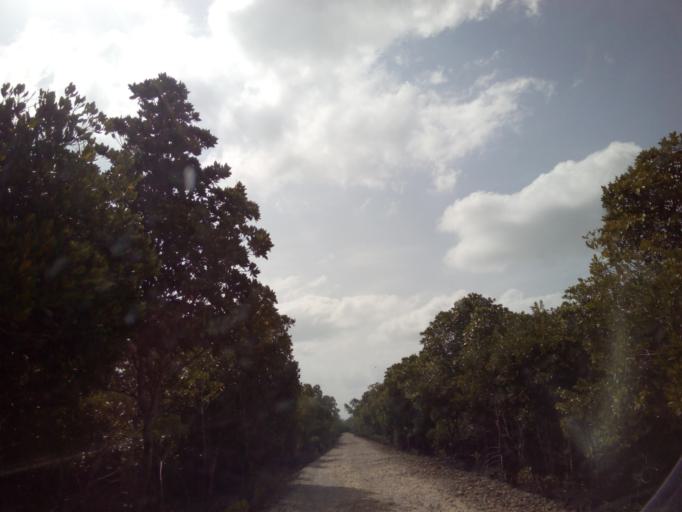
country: TZ
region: Zanzibar Central/South
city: Mahonda
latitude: -6.3142
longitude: 39.3835
